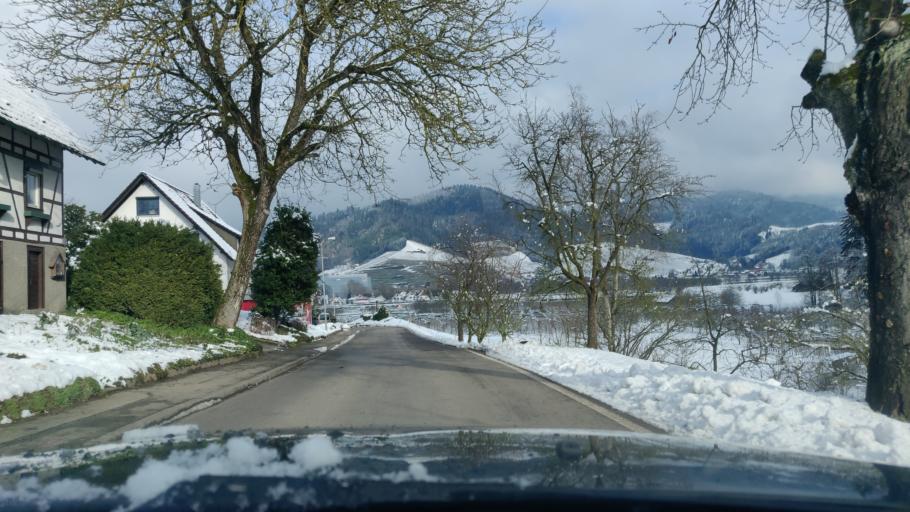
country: DE
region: Baden-Wuerttemberg
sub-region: Freiburg Region
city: Oberkirch
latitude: 48.5168
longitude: 8.0828
